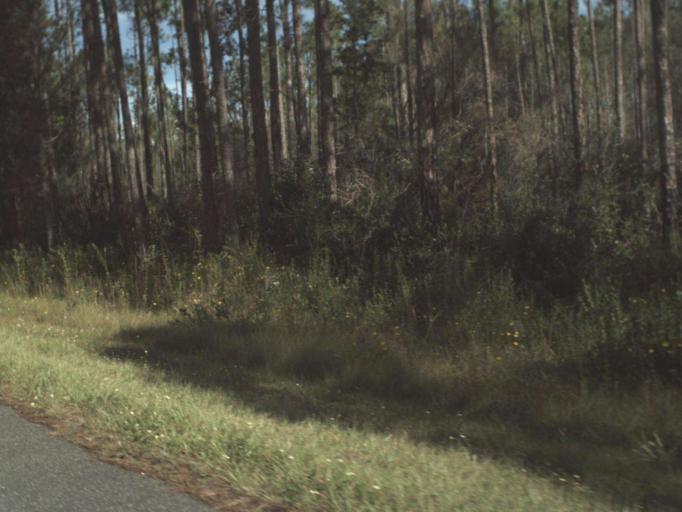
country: US
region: Florida
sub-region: Franklin County
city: Apalachicola
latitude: 29.8494
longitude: -84.9721
